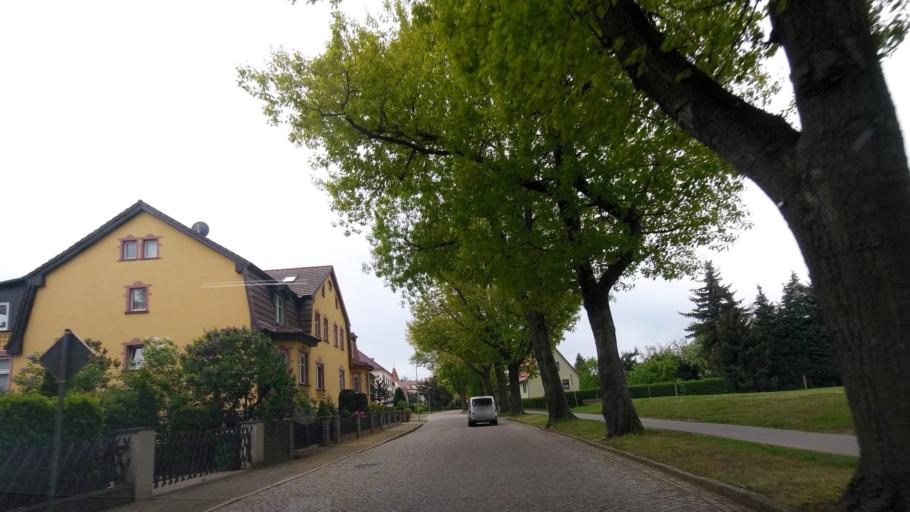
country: DE
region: Brandenburg
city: Dahme
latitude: 51.8699
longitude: 13.4339
